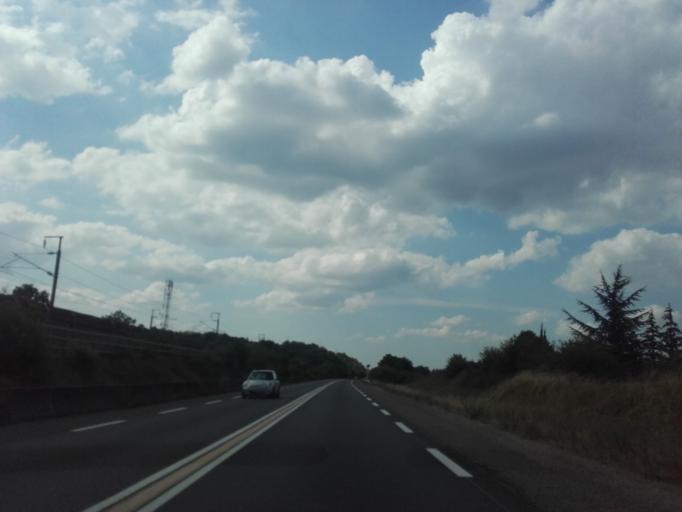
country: FR
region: Bourgogne
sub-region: Departement de Saone-et-Loire
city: Prisse
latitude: 46.3178
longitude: 4.7439
